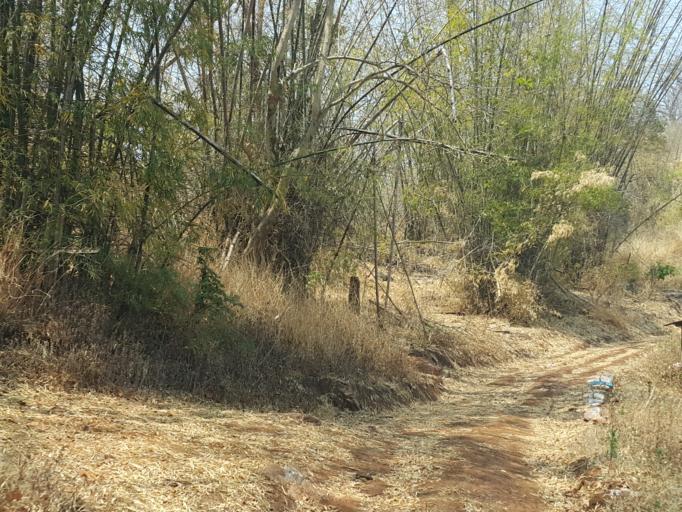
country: TH
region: Chiang Mai
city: Samoeng
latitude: 18.7816
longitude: 98.8223
